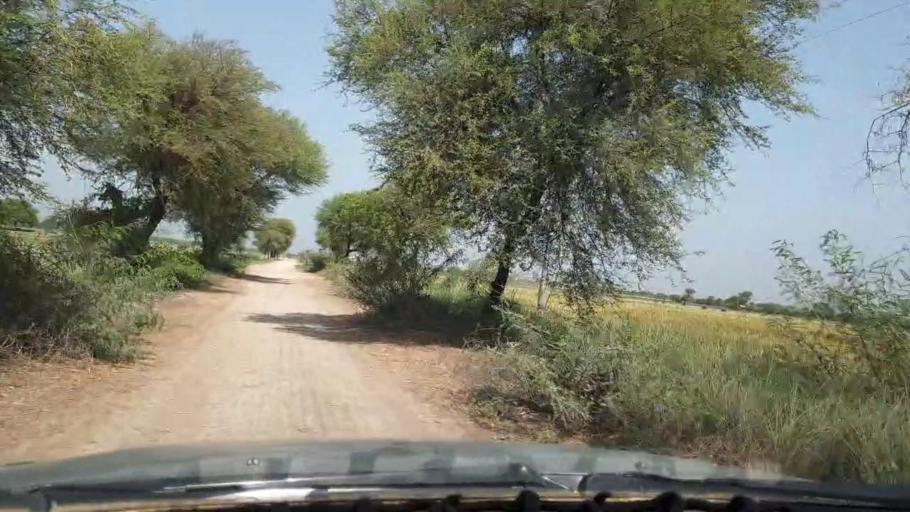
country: PK
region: Sindh
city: Tando Muhammad Khan
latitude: 25.1539
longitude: 68.6337
